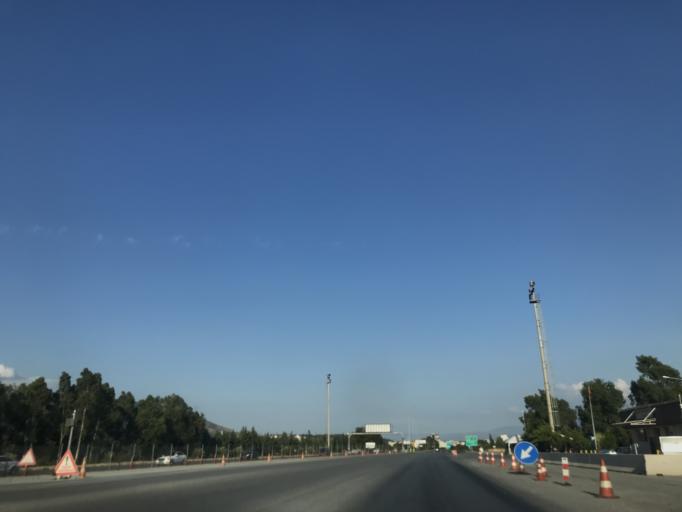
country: TR
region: Aydin
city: Aydin
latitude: 37.8602
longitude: 27.7893
